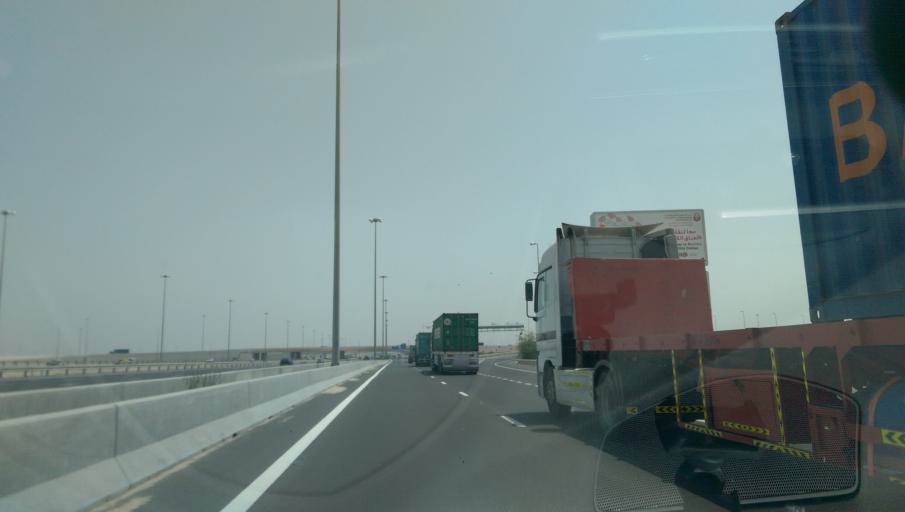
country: AE
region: Abu Dhabi
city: Abu Dhabi
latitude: 24.6898
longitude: 54.7763
